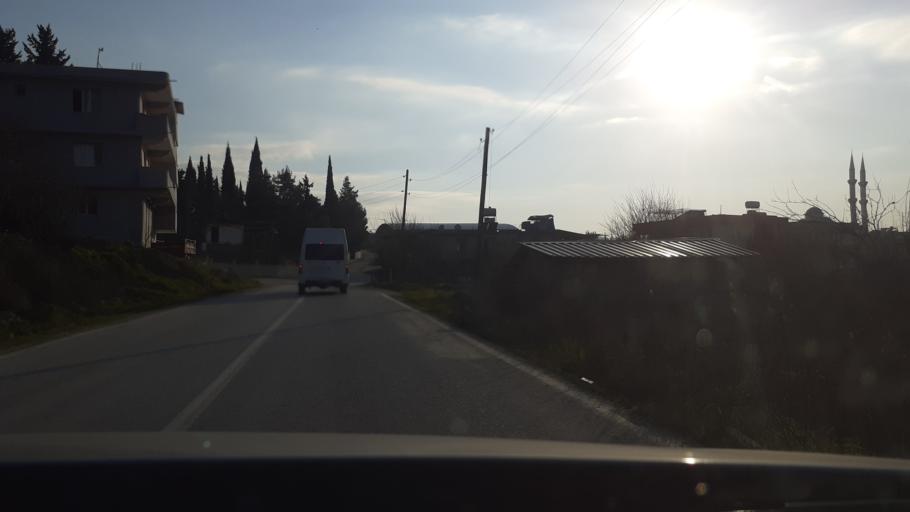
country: TR
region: Hatay
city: Oymakli
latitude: 36.1138
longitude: 36.3014
